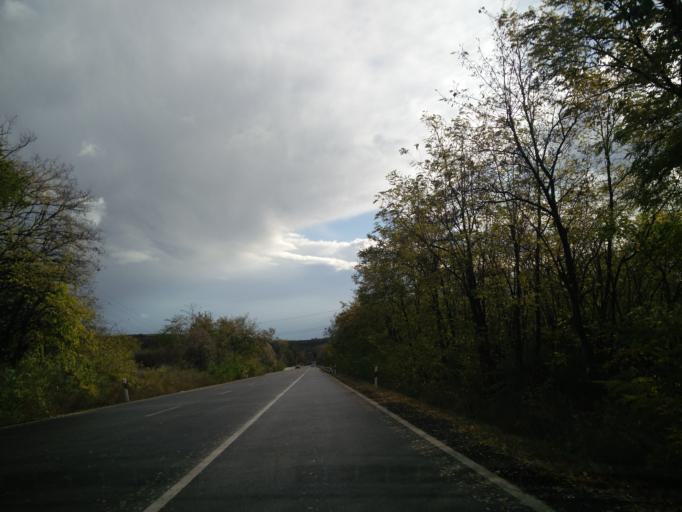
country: HU
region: Pest
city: Kerepes
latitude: 47.5751
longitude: 19.2919
